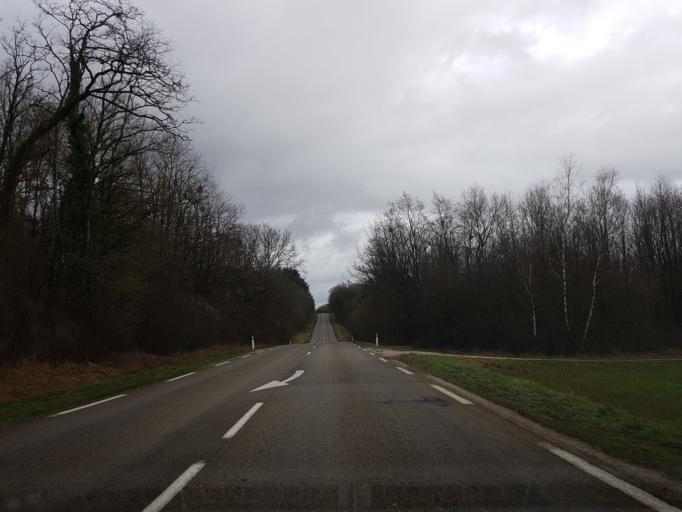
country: FR
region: Franche-Comte
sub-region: Departement de la Haute-Saone
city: Scey-sur-Saone-et-Saint-Albin
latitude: 47.6952
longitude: 5.9695
